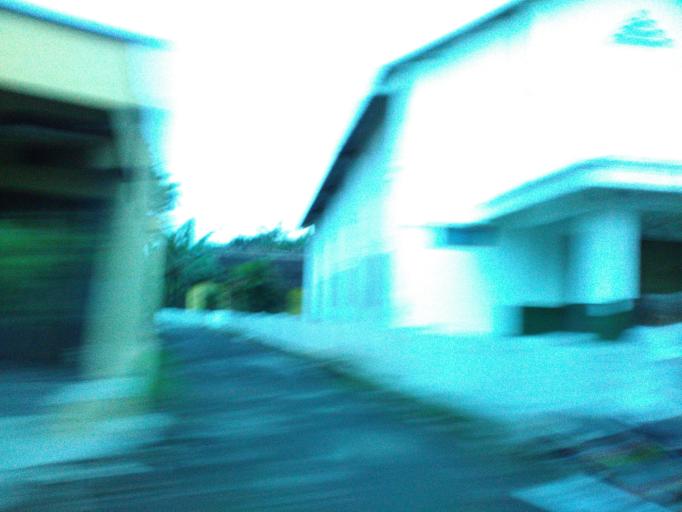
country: ID
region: Central Java
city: Ceper
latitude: -7.6500
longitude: 110.6839
